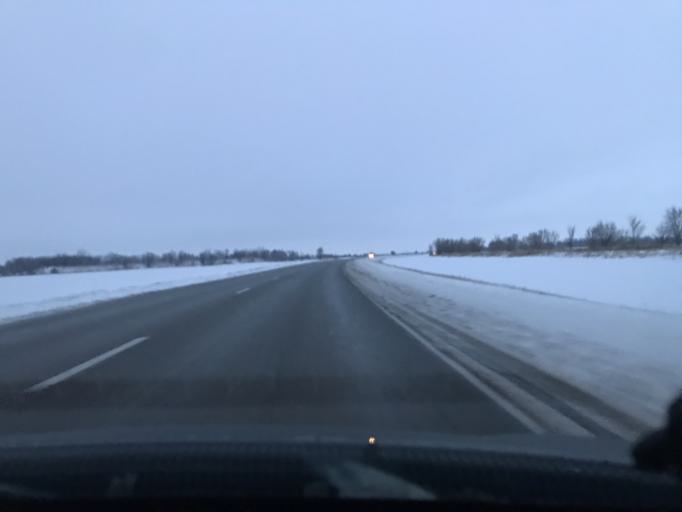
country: RU
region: Rostov
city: Letnik
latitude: 45.9450
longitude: 41.2867
